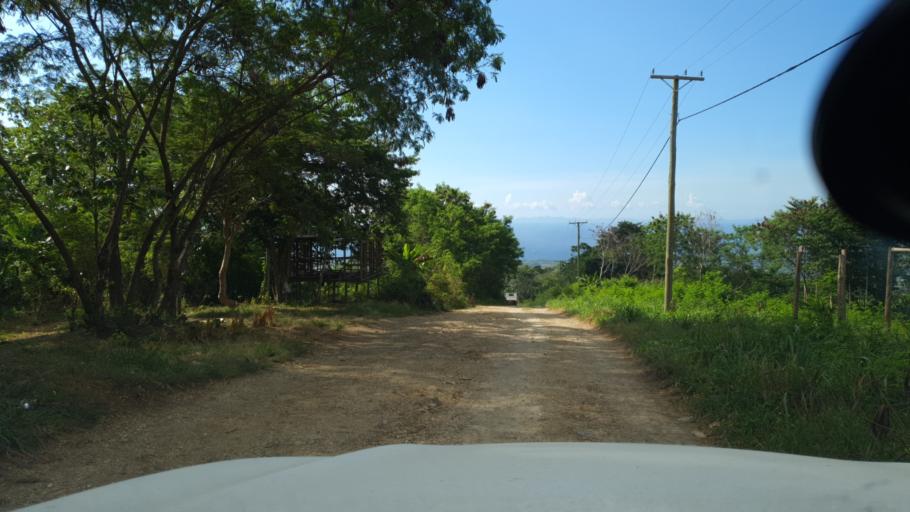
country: SB
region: Guadalcanal
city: Honiara
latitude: -9.4666
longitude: 159.9745
